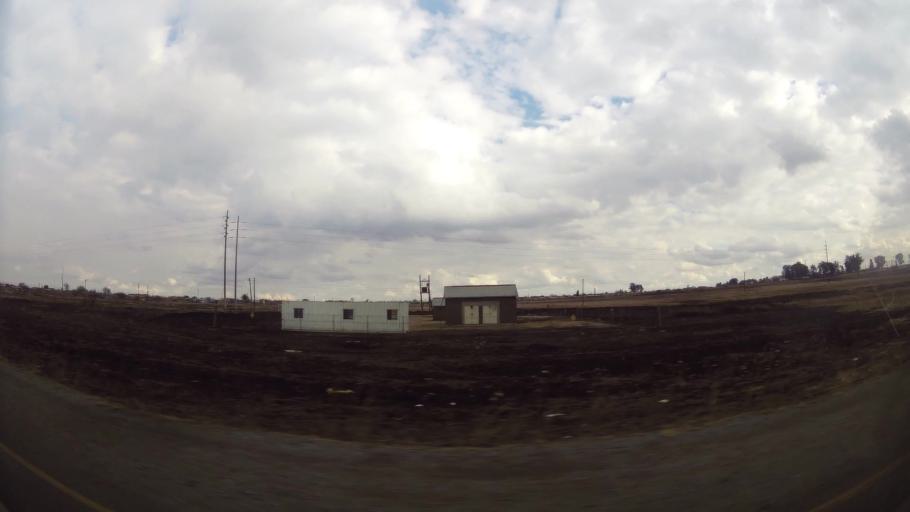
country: ZA
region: Orange Free State
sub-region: Fezile Dabi District Municipality
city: Sasolburg
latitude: -26.8431
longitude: 27.8821
